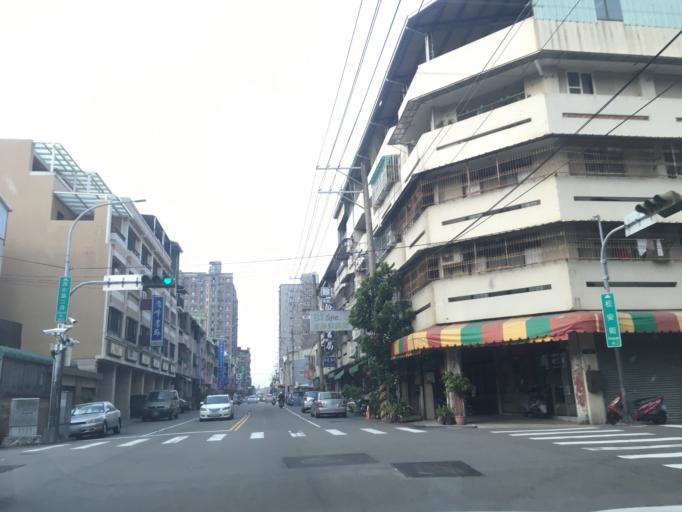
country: TW
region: Taiwan
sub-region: Taichung City
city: Taichung
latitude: 24.1811
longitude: 120.6950
